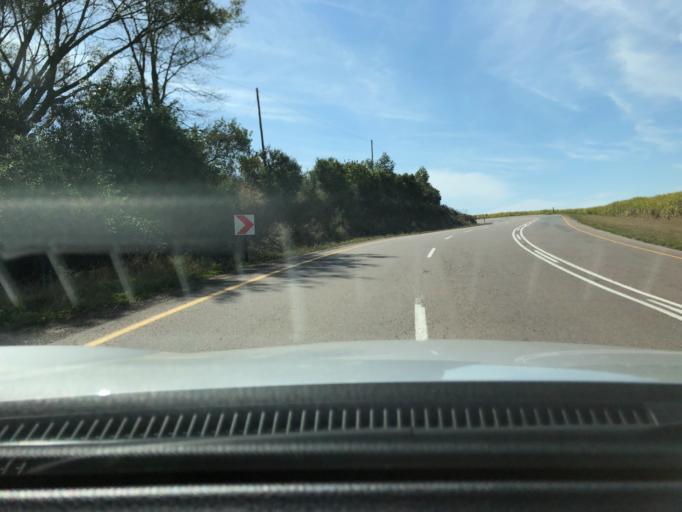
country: ZA
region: KwaZulu-Natal
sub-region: uMgungundlovu District Municipality
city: Richmond
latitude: -29.8176
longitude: 30.3425
